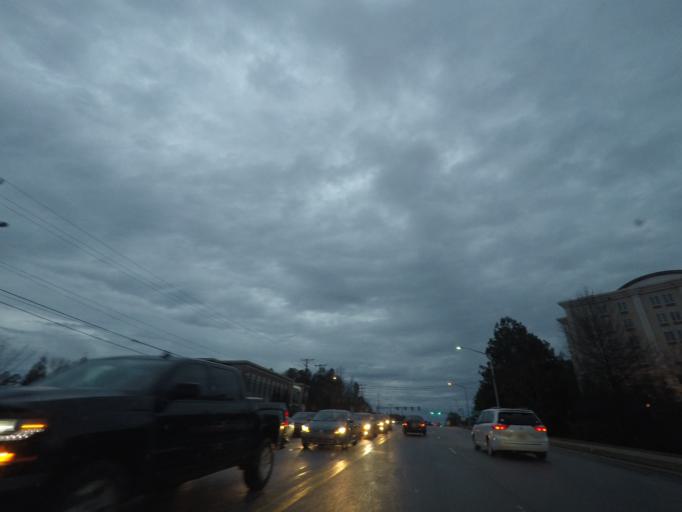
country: US
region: North Carolina
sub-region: Orange County
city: Chapel Hill
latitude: 35.9012
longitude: -78.9596
